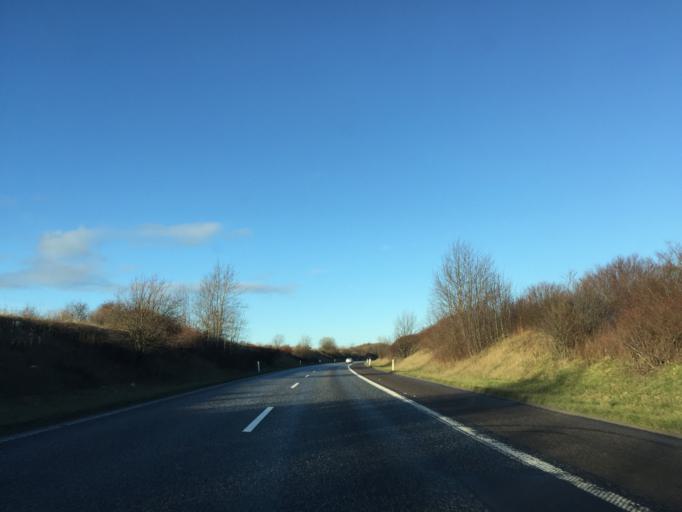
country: DK
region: South Denmark
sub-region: Fredericia Kommune
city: Taulov
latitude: 55.5974
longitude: 9.5904
